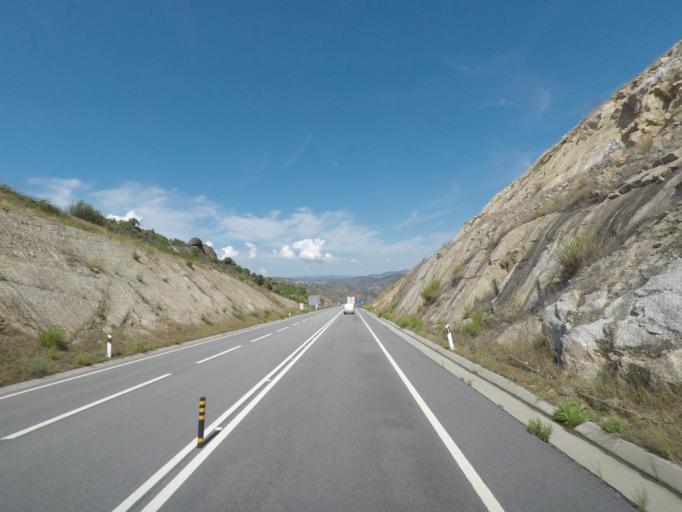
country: PT
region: Braganca
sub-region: Carrazeda de Ansiaes
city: Carrazeda de Anciaes
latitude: 41.3104
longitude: -7.3467
